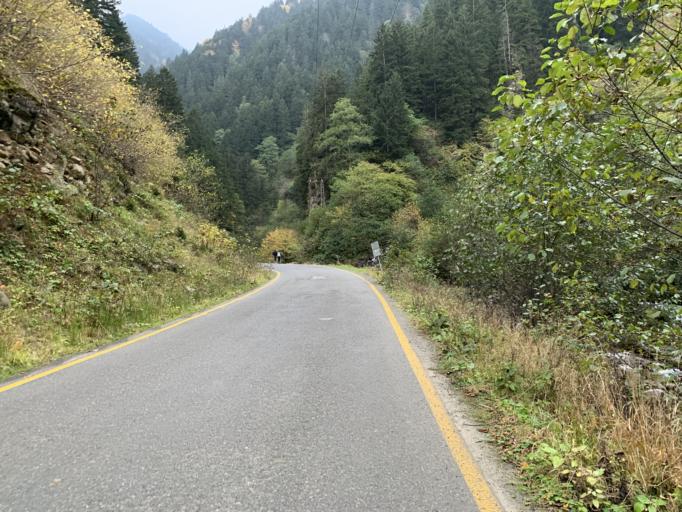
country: TR
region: Trabzon
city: Uzungol
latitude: 40.5936
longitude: 40.3211
